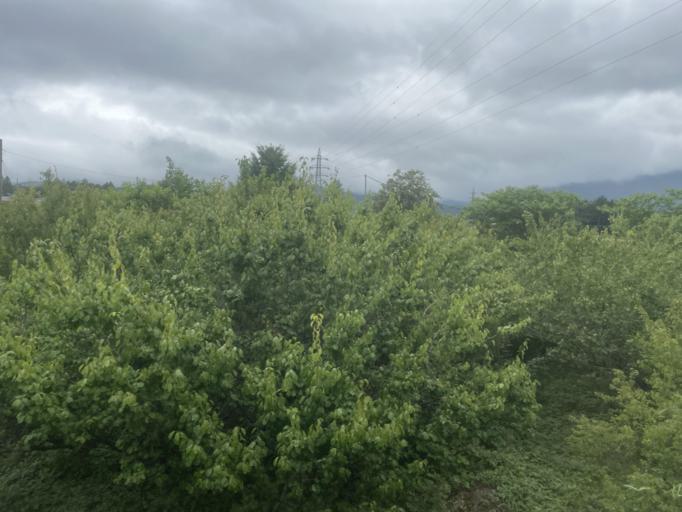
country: JP
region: Saitama
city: Chichibu
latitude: 36.0297
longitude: 139.0973
